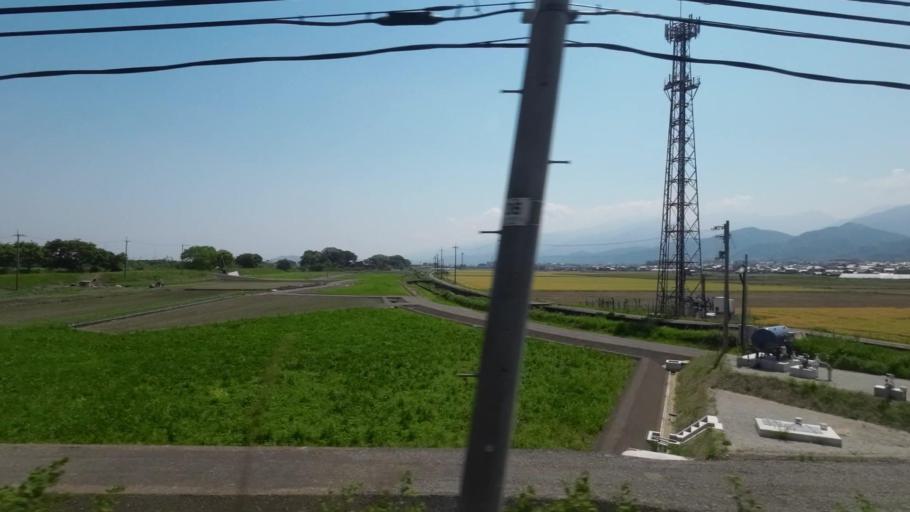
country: JP
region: Ehime
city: Saijo
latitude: 33.9041
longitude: 133.0994
